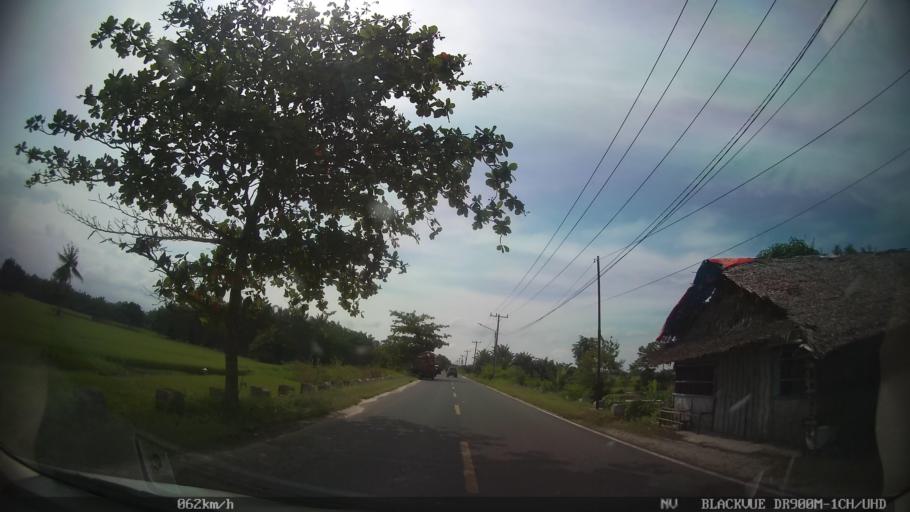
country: ID
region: North Sumatra
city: Percut
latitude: 3.6126
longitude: 98.8449
